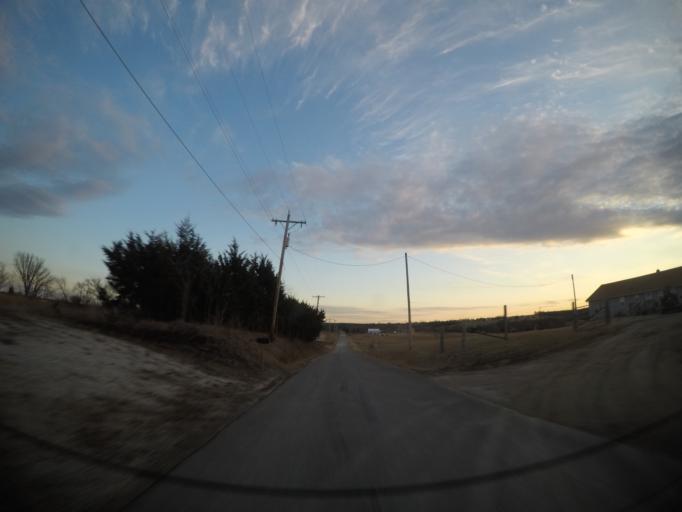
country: US
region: Kansas
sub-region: Wyandotte County
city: Bonner Springs
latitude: 39.0391
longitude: -94.9089
